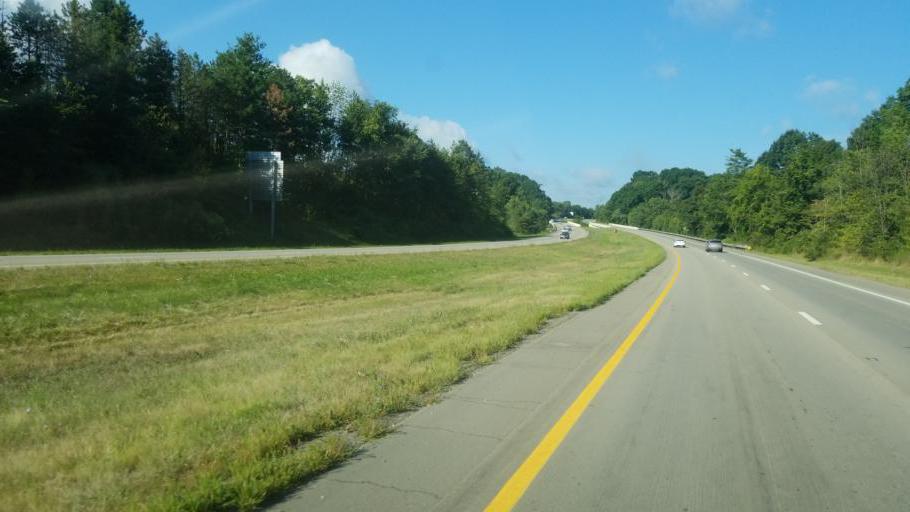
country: US
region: Ohio
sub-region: Stark County
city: Navarre
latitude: 40.7599
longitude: -81.5296
